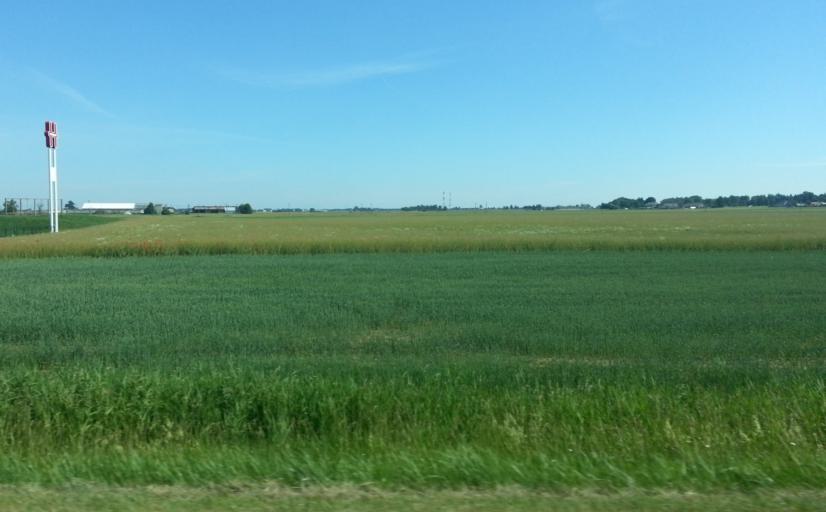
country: LT
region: Panevezys
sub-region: Panevezys City
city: Panevezys
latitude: 55.6688
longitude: 24.3515
